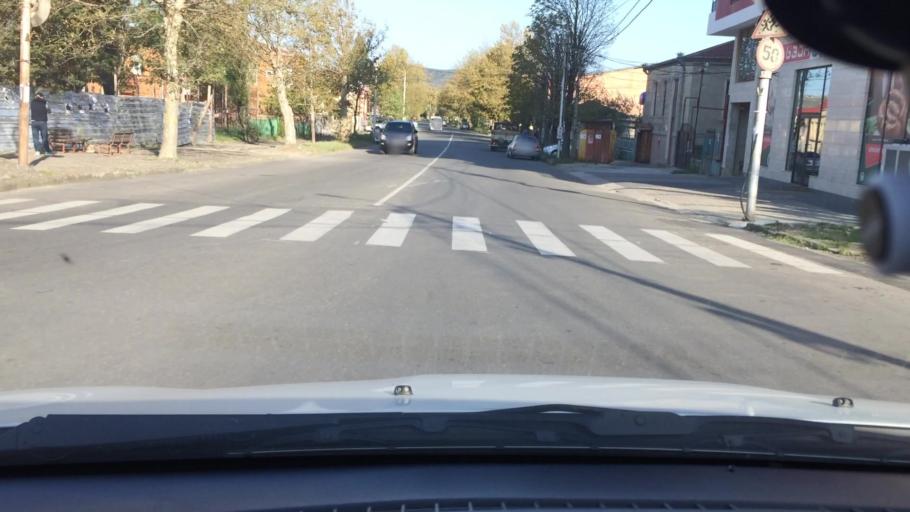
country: GE
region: Imereti
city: Kutaisi
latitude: 42.2664
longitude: 42.7180
